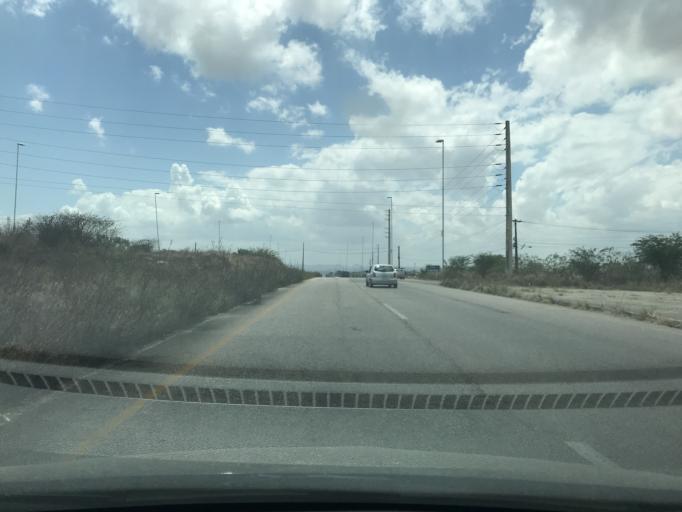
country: BR
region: Pernambuco
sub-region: Caruaru
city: Caruaru
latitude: -8.3055
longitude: -35.9661
